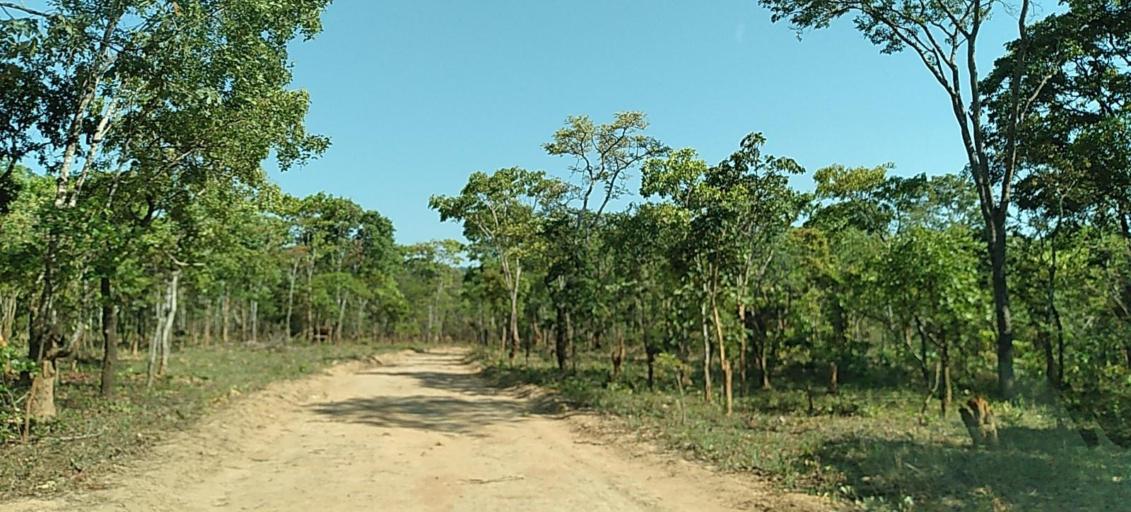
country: ZM
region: Central
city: Mkushi
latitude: -13.4738
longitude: 28.9806
